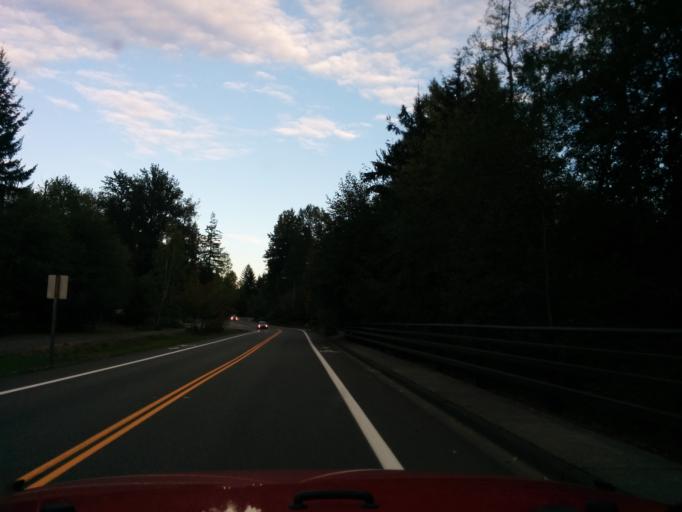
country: US
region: Washington
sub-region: King County
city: Union Hill-Novelty Hill
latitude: 47.6769
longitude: -122.0267
